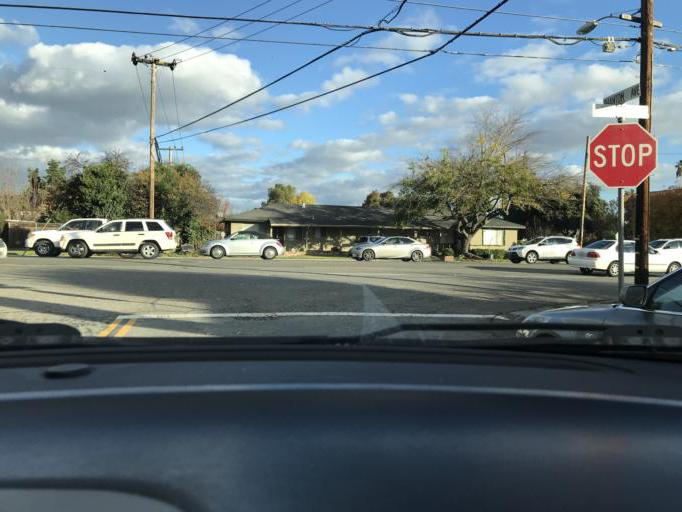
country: US
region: California
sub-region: Santa Clara County
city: Buena Vista
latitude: 37.2942
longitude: -121.9204
